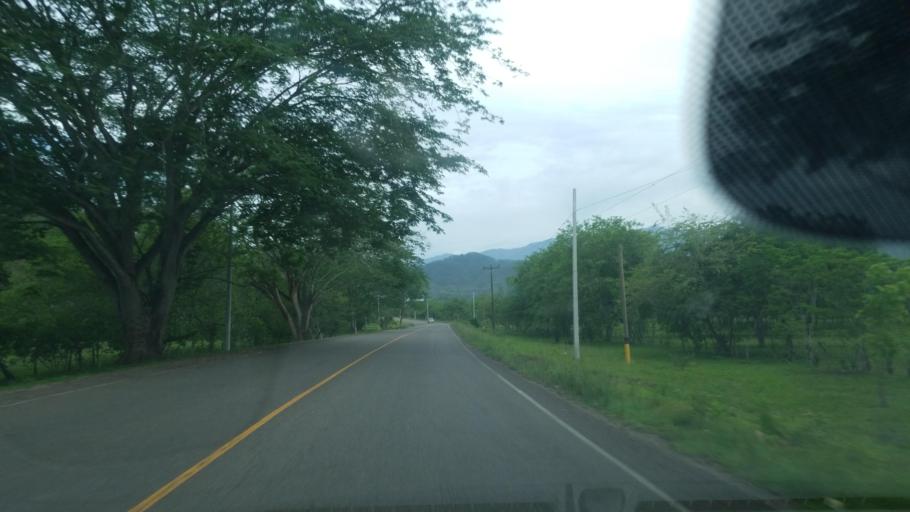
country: HN
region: Santa Barbara
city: San Vicente Centenario
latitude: 14.8725
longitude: -88.2481
